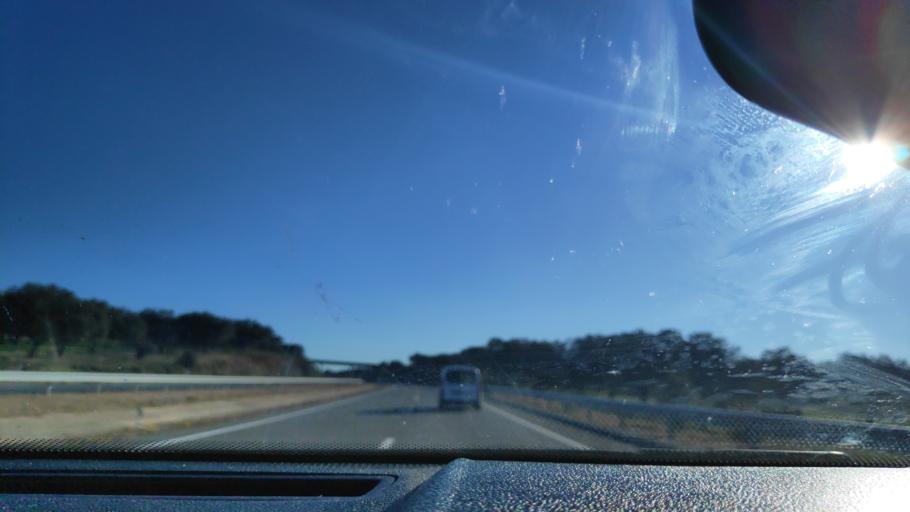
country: ES
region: Andalusia
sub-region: Provincia de Huelva
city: Santa Olalla del Cala
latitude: 37.9735
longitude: -6.2359
